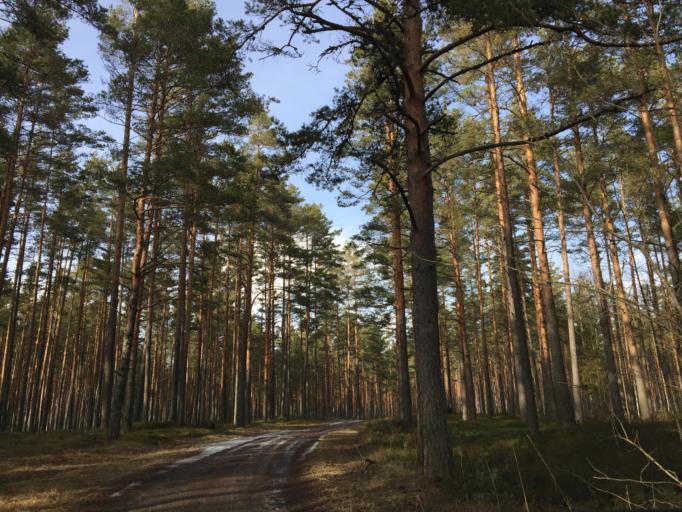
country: EE
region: Paernumaa
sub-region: Paernu linn
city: Parnu
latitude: 58.2354
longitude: 24.5188
